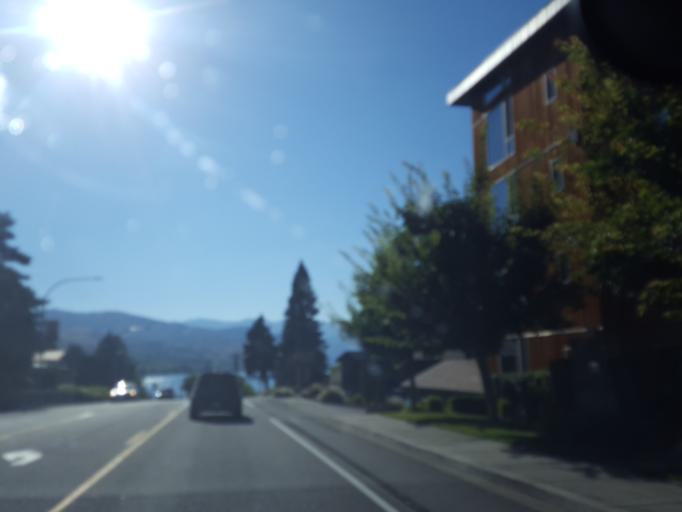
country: US
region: Washington
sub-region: Chelan County
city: Chelan
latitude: 47.8360
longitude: -120.0534
